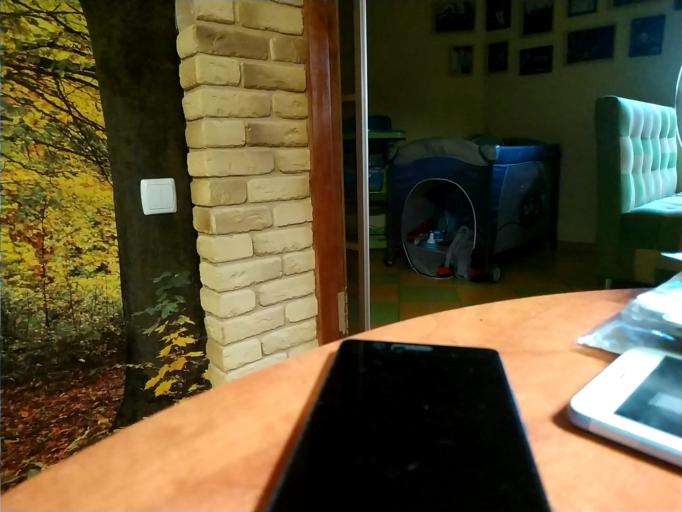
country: RU
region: Orjol
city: Znamenskoye
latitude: 53.5135
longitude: 35.5022
